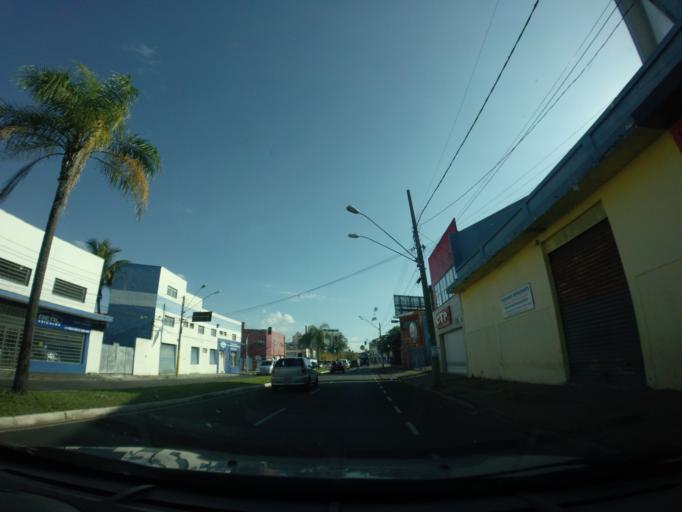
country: BR
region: Sao Paulo
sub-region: Rio Claro
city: Rio Claro
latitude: -22.4070
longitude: -47.5646
